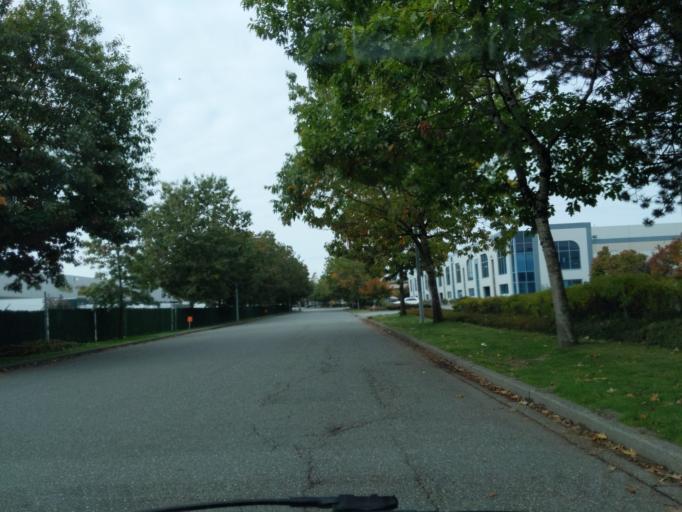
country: CA
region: British Columbia
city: Walnut Grove
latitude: 49.1848
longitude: -122.6606
